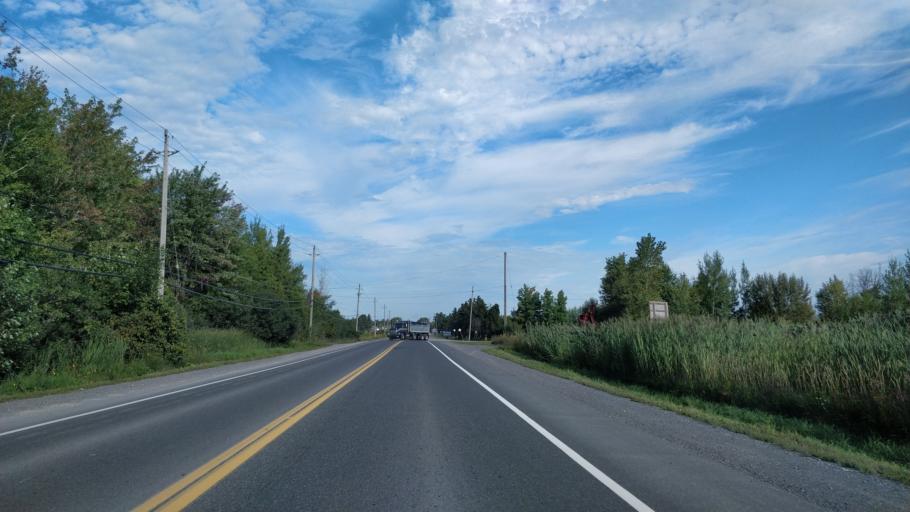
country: CA
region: Ontario
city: Bells Corners
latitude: 45.2900
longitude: -75.9682
